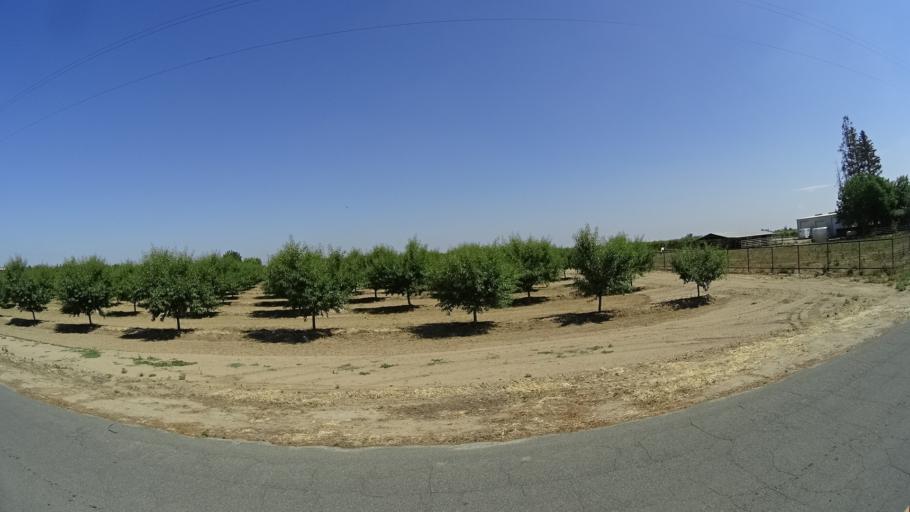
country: US
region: California
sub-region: Fresno County
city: Kingsburg
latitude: 36.4596
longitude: -119.5725
